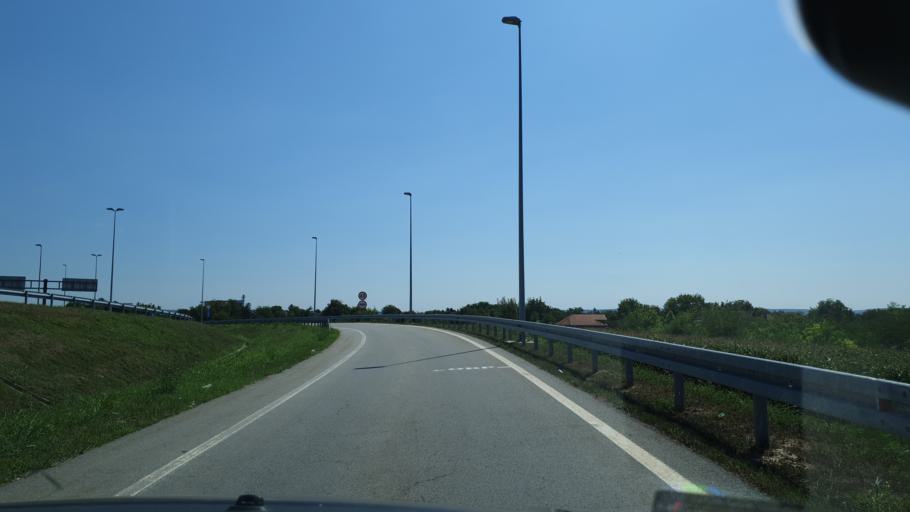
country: RS
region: Autonomna Pokrajina Vojvodina
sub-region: Juznobacki Okrug
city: Kovilj
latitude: 45.2421
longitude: 20.0335
